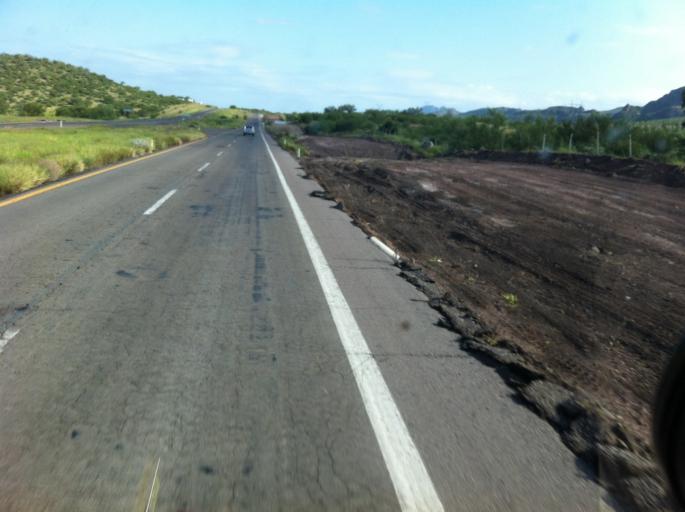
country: MX
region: Sonora
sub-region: Empalme
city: La Palma
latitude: 28.4852
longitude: -111.0444
